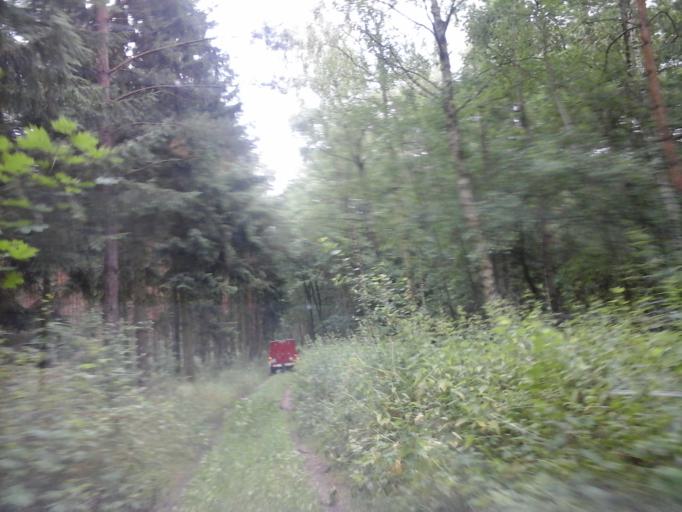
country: PL
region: West Pomeranian Voivodeship
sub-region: Powiat choszczenski
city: Krzecin
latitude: 52.9956
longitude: 15.5545
